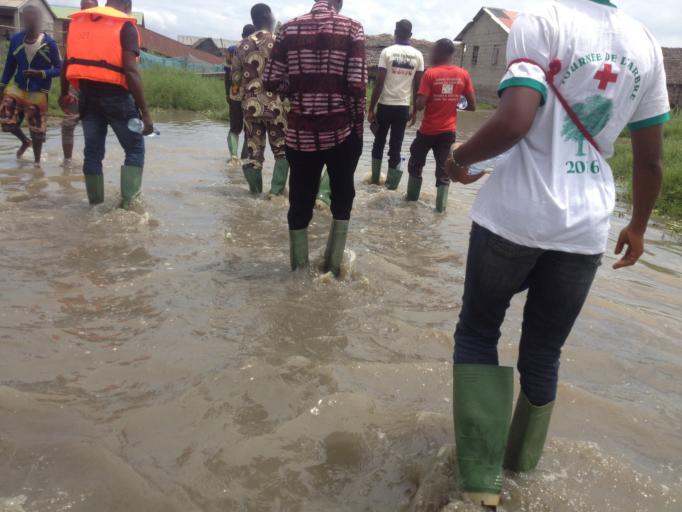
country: BJ
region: Queme
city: Porto-Novo
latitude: 6.4458
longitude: 2.5427
